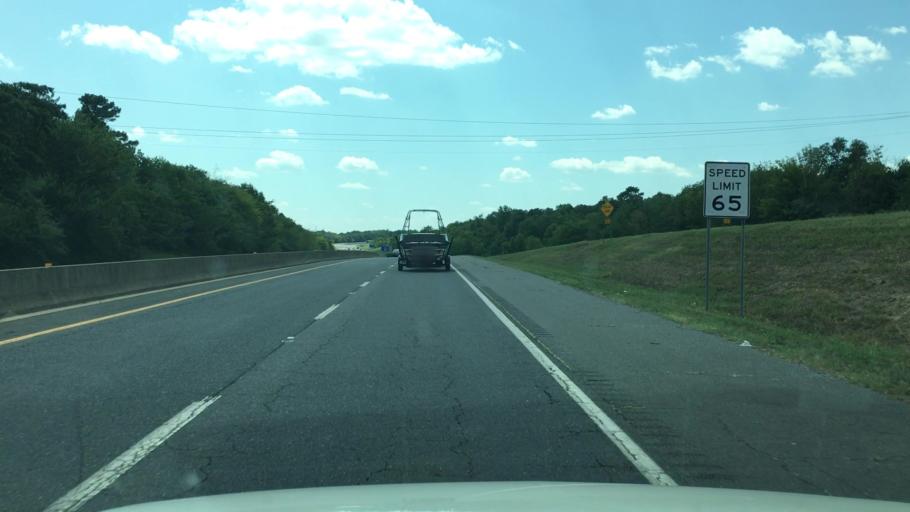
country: US
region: Arkansas
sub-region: Garland County
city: Rockwell
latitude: 34.4713
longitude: -93.0973
